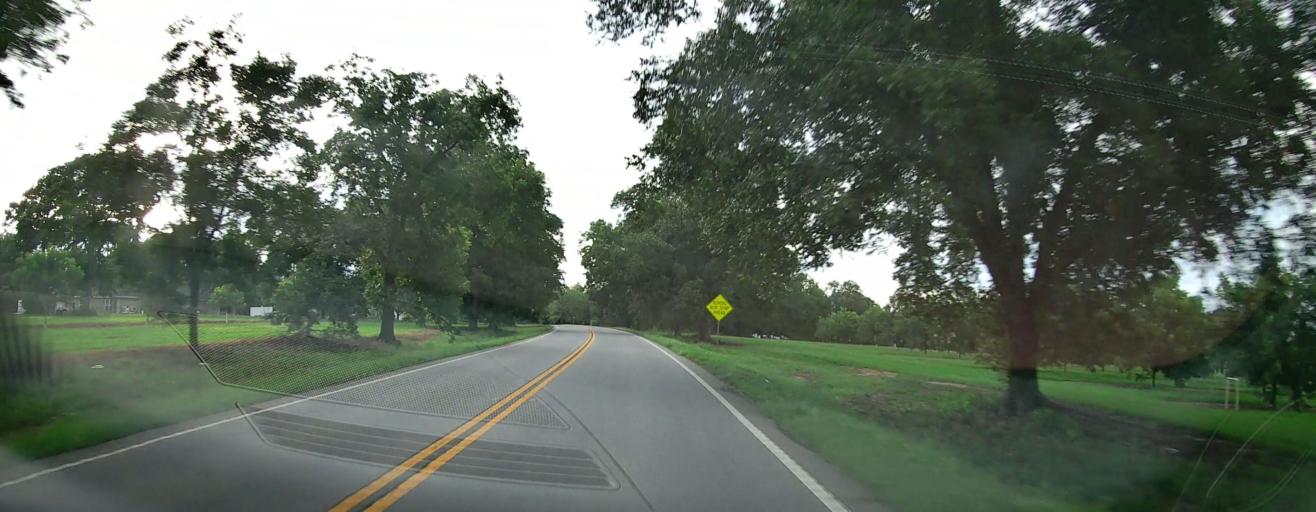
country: US
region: Georgia
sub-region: Houston County
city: Perry
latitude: 32.4498
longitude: -83.6677
